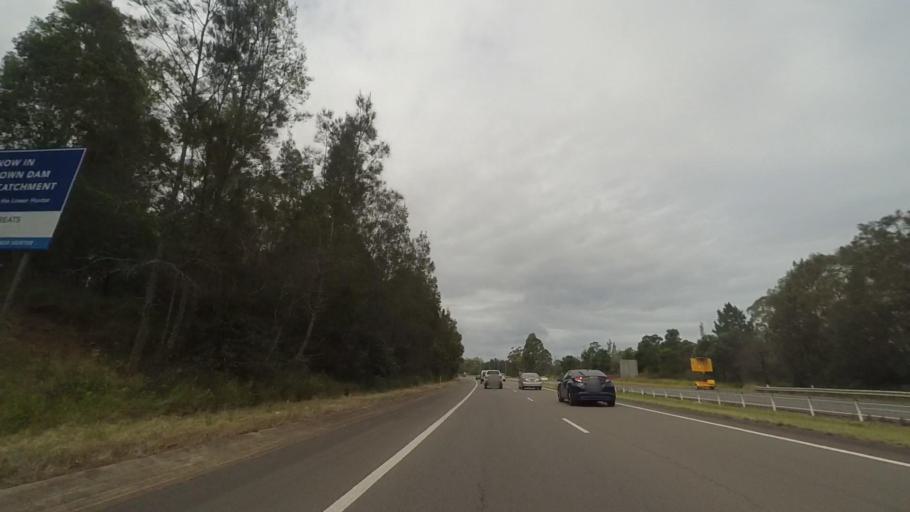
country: AU
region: New South Wales
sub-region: Port Stephens Shire
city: Raymond Terrace
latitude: -32.7442
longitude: 151.7733
